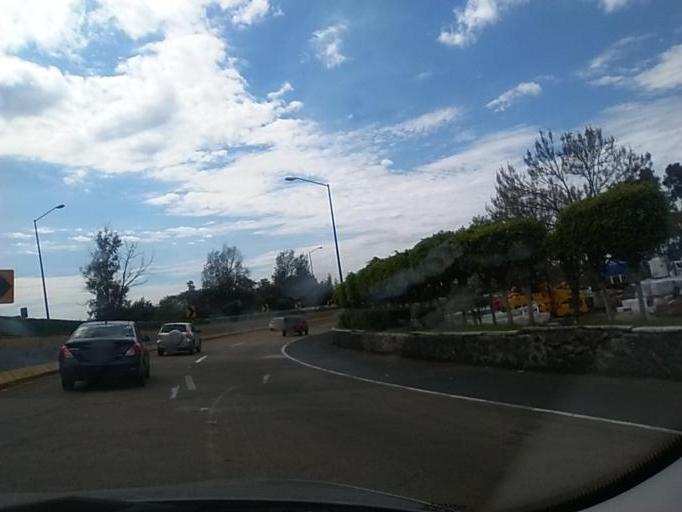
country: MX
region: Morelos
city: Tepoztlan
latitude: 19.0209
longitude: -99.1366
